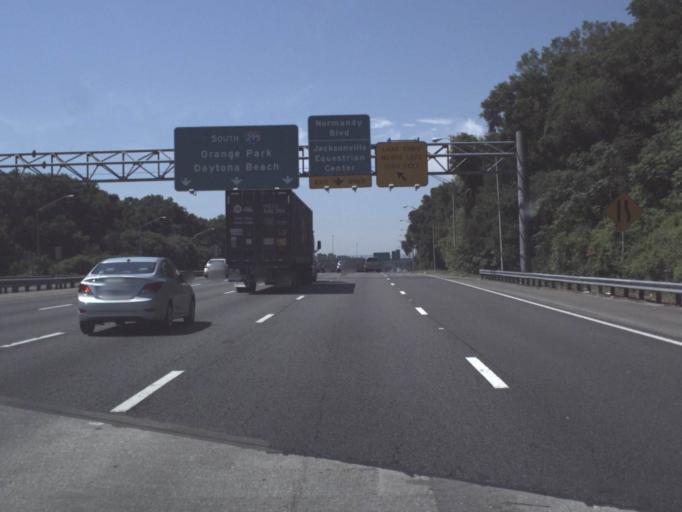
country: US
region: Florida
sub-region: Duval County
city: Jacksonville
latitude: 30.3056
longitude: -81.7705
